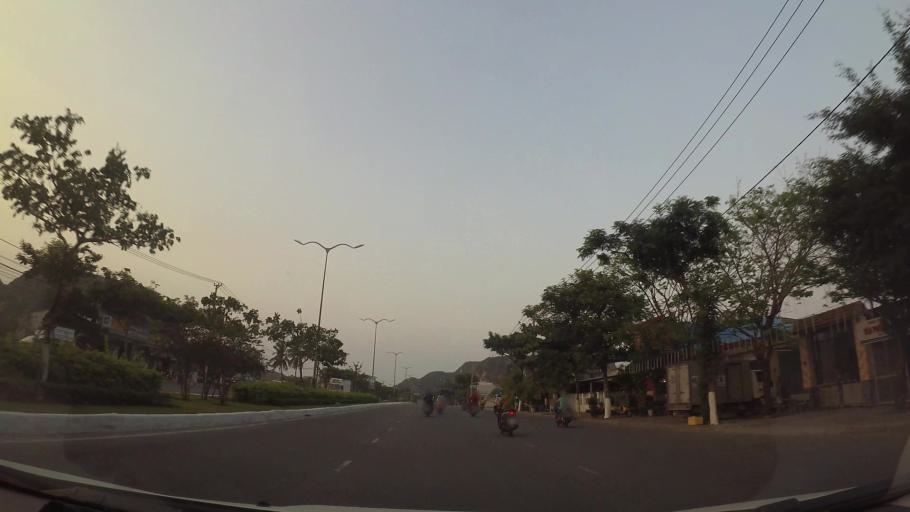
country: VN
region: Da Nang
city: Ngu Hanh Son
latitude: 15.9960
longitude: 108.2590
